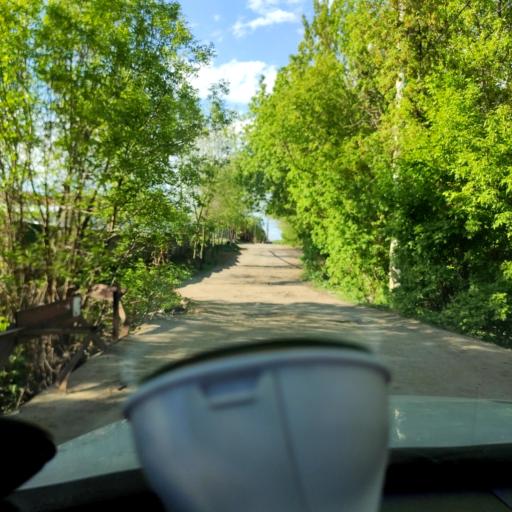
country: RU
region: Samara
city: Petra-Dubrava
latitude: 53.2567
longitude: 50.3440
